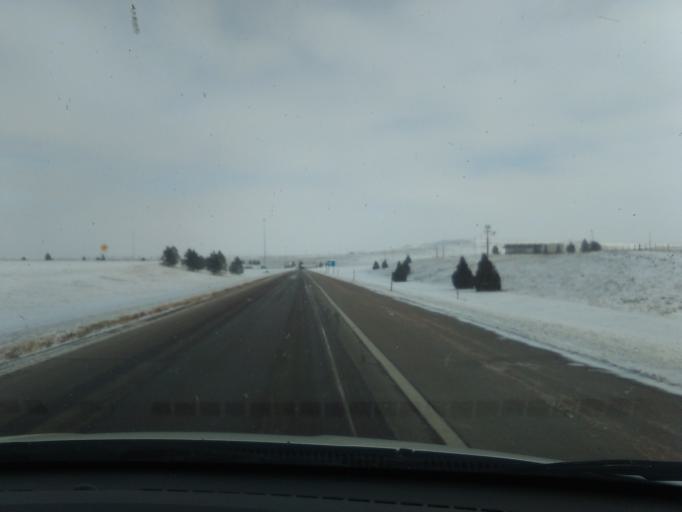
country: US
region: Nebraska
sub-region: Kimball County
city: Kimball
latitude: 41.2154
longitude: -103.6689
